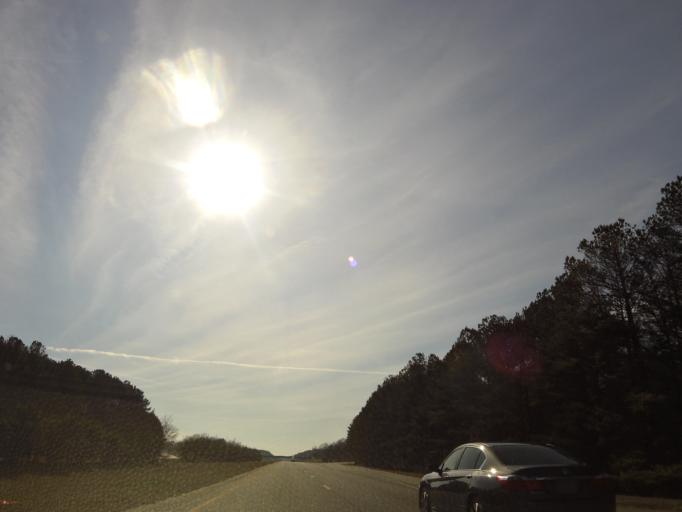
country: US
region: Georgia
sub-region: Harris County
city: Pine Mountain
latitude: 32.8614
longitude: -84.9734
